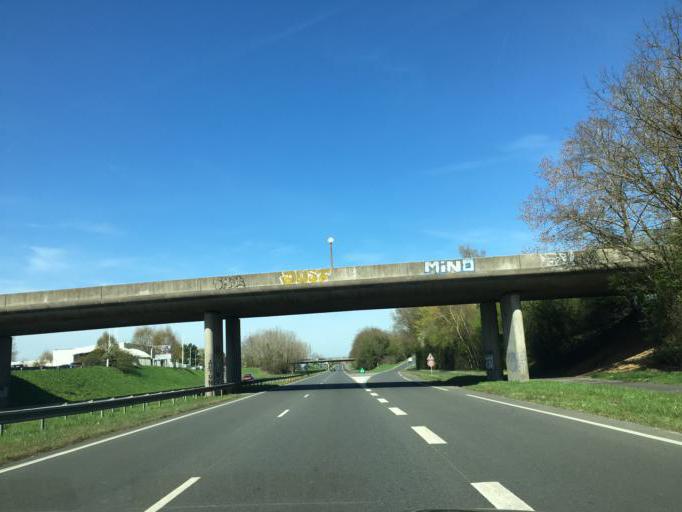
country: FR
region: Ile-de-France
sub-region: Departement de l'Essonne
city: Evry
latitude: 48.6378
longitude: 2.4319
